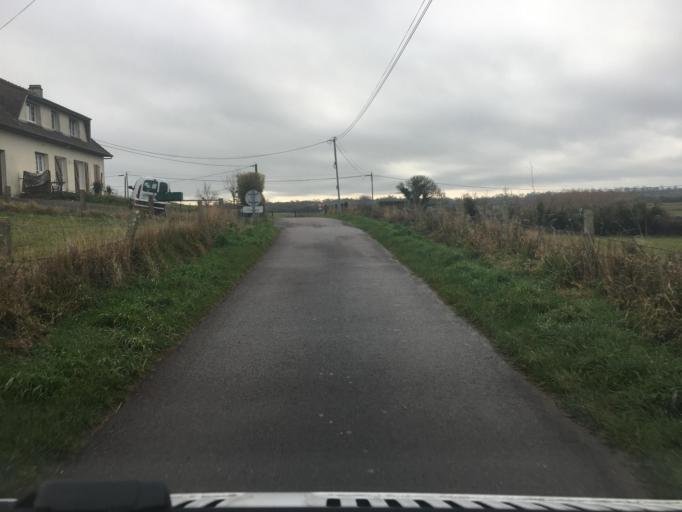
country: FR
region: Lower Normandy
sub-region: Departement du Calvados
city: Grandcamp-Maisy
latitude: 49.3903
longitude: -1.0194
